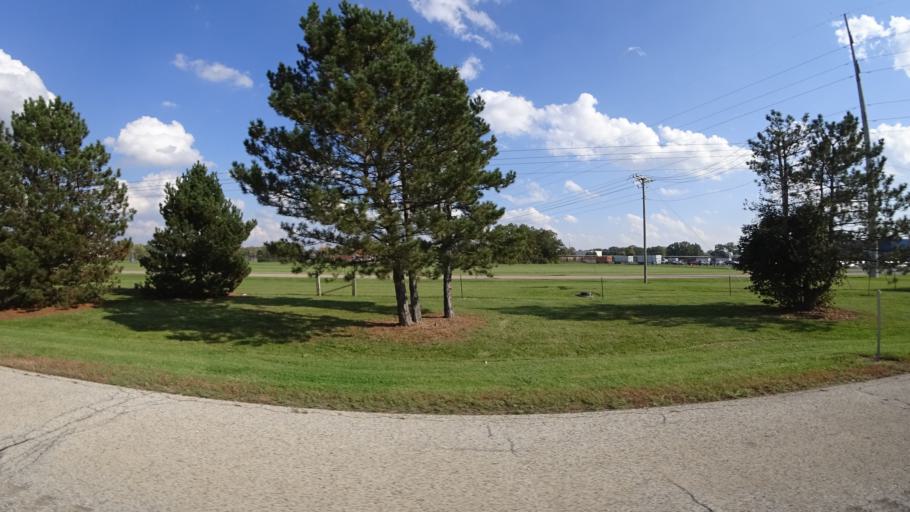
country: US
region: Michigan
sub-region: Saint Joseph County
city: Three Rivers
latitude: 41.9621
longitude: -85.6415
